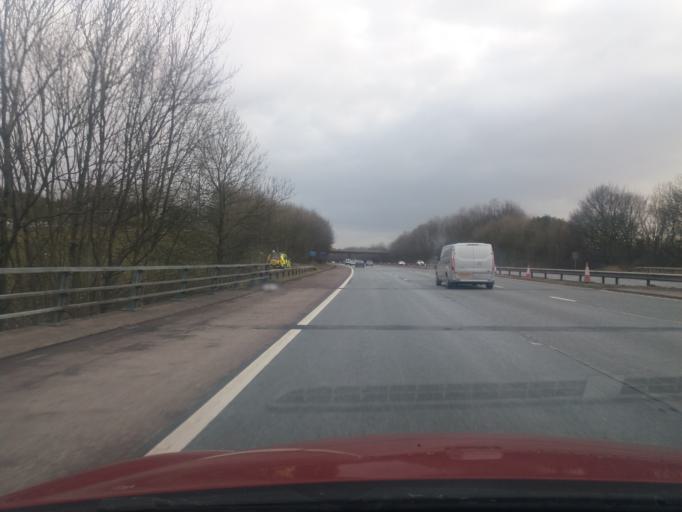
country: GB
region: England
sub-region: Lancashire
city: Chorley
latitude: 53.6832
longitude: -2.6265
